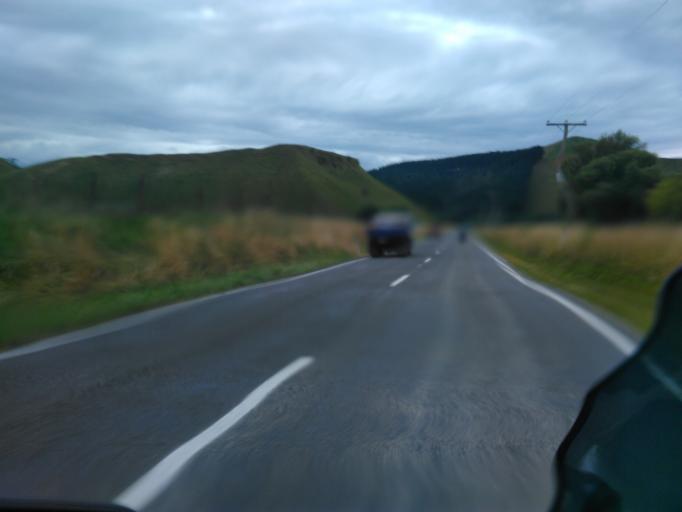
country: NZ
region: Gisborne
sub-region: Gisborne District
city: Gisborne
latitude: -38.4623
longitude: 177.7387
